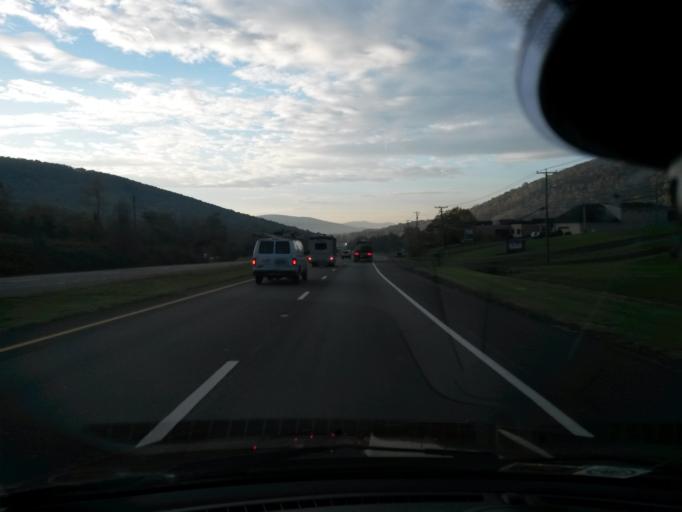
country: US
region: Virginia
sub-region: Botetourt County
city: Cloverdale
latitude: 37.3589
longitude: -79.8855
